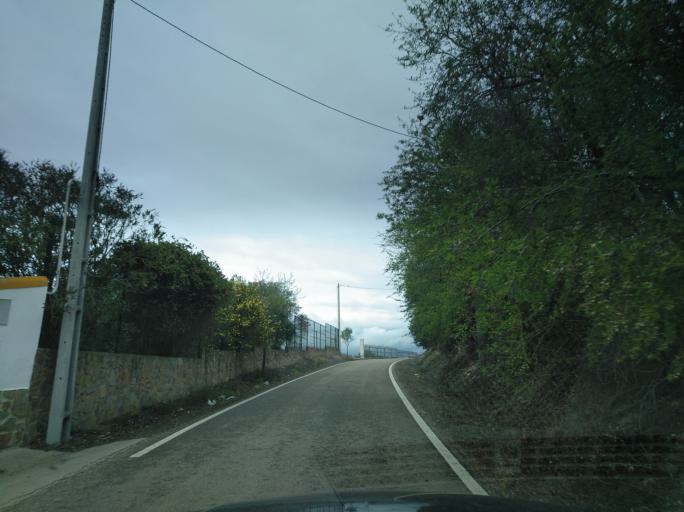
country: PT
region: Portalegre
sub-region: Campo Maior
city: Campo Maior
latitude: 38.9915
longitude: -7.0481
